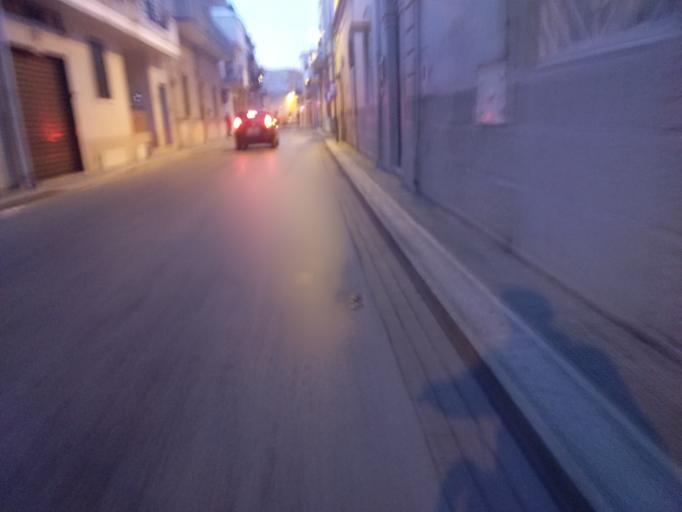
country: IT
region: Apulia
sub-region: Provincia di Bari
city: Modugno
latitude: 41.0796
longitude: 16.7804
